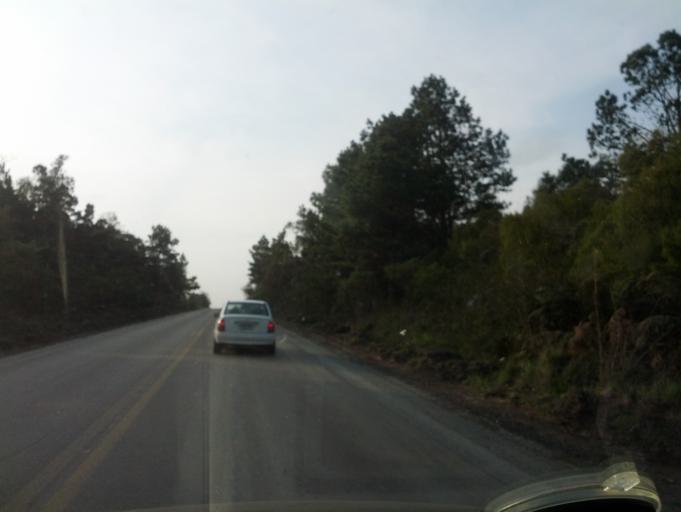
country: BR
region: Santa Catarina
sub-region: Otacilio Costa
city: Otacilio Costa
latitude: -27.4523
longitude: -50.1229
